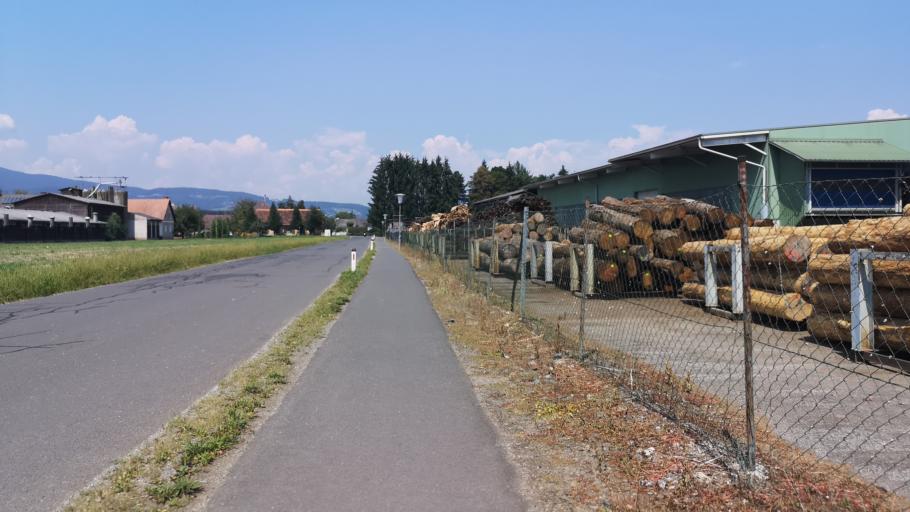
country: AT
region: Styria
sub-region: Politischer Bezirk Deutschlandsberg
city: Deutschlandsberg
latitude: 46.8199
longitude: 15.2560
